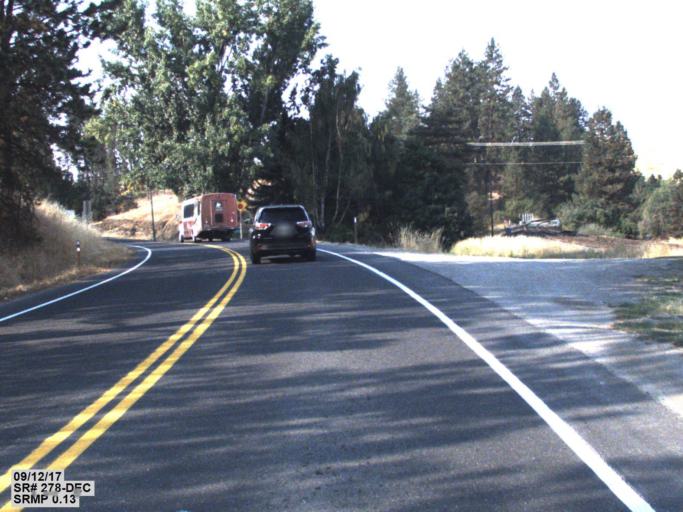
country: US
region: Washington
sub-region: Spokane County
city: Veradale
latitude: 47.4513
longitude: -117.1396
